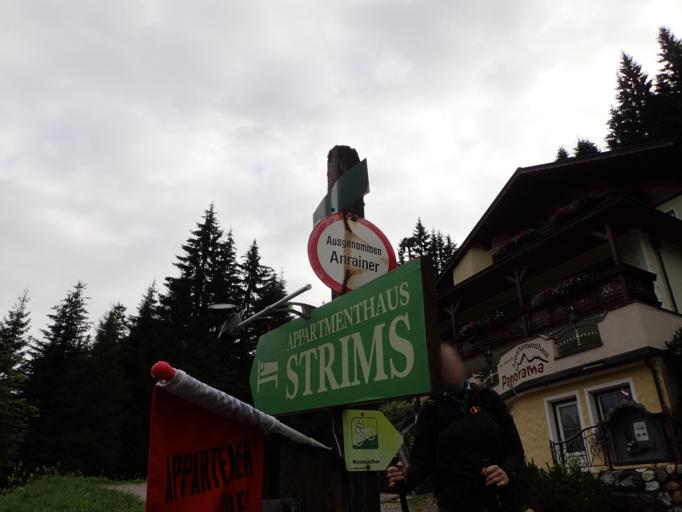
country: AT
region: Salzburg
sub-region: Politischer Bezirk Sankt Johann im Pongau
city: Untertauern
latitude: 47.2981
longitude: 13.4574
